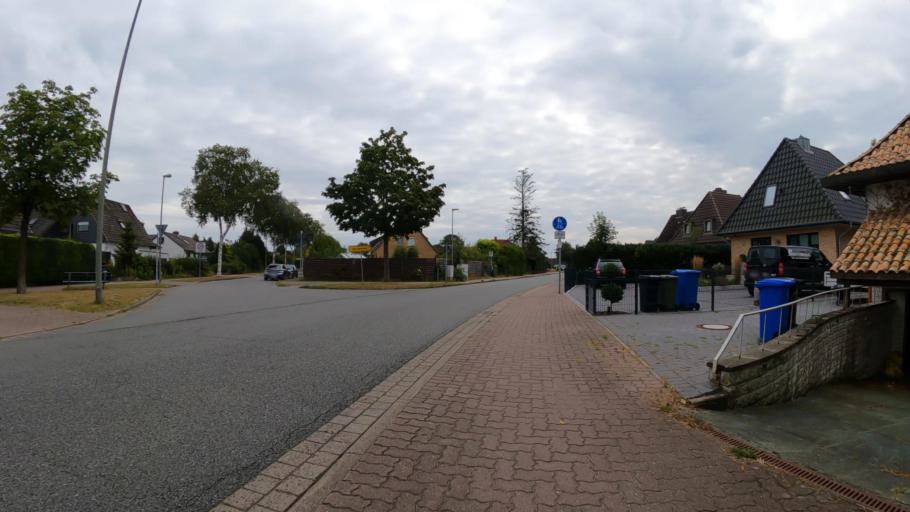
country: DE
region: Schleswig-Holstein
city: Boostedt
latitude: 54.0524
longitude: 10.0308
